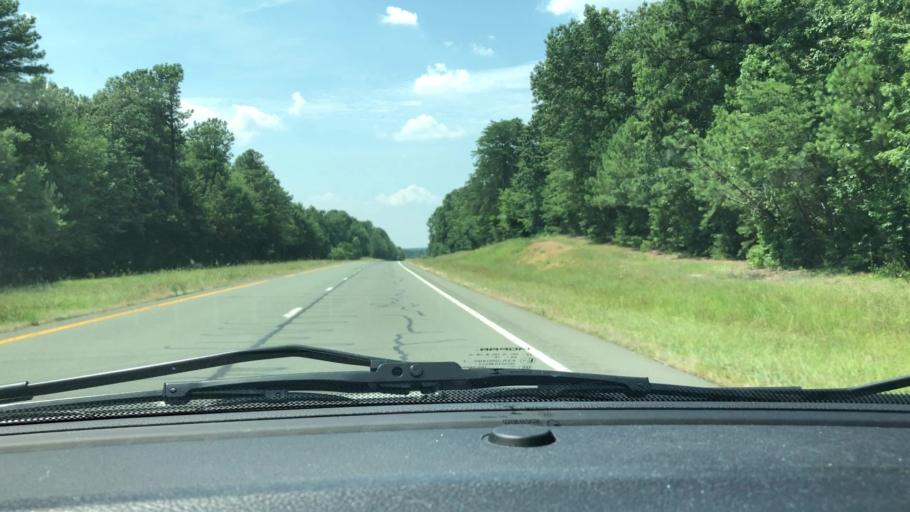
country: US
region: North Carolina
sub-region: Chatham County
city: Siler City
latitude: 35.7855
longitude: -79.5182
